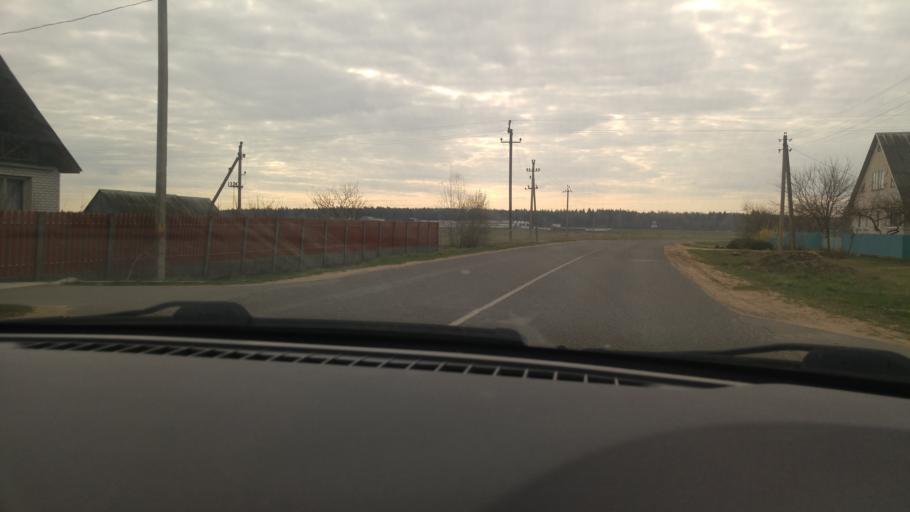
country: BY
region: Minsk
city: Chervyen'
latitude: 53.6946
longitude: 28.4349
